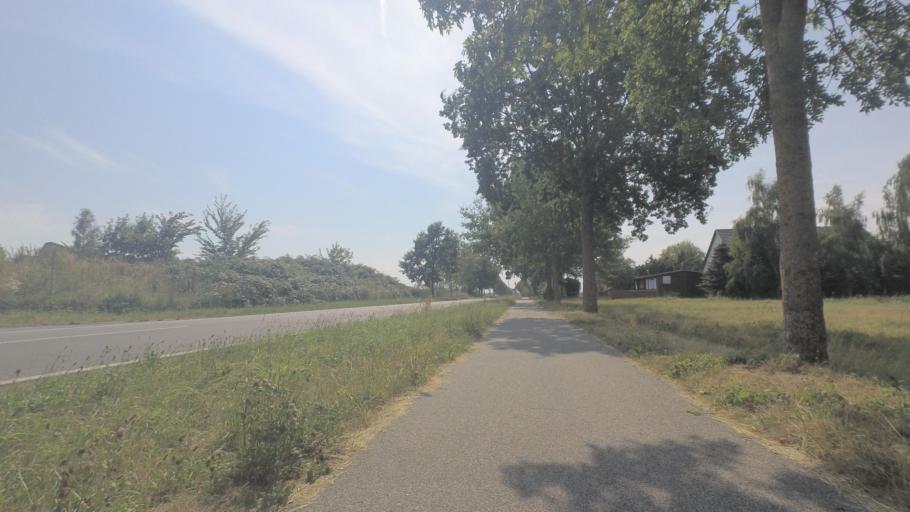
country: DE
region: Mecklenburg-Vorpommern
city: Poseritz
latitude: 54.2279
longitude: 13.2720
